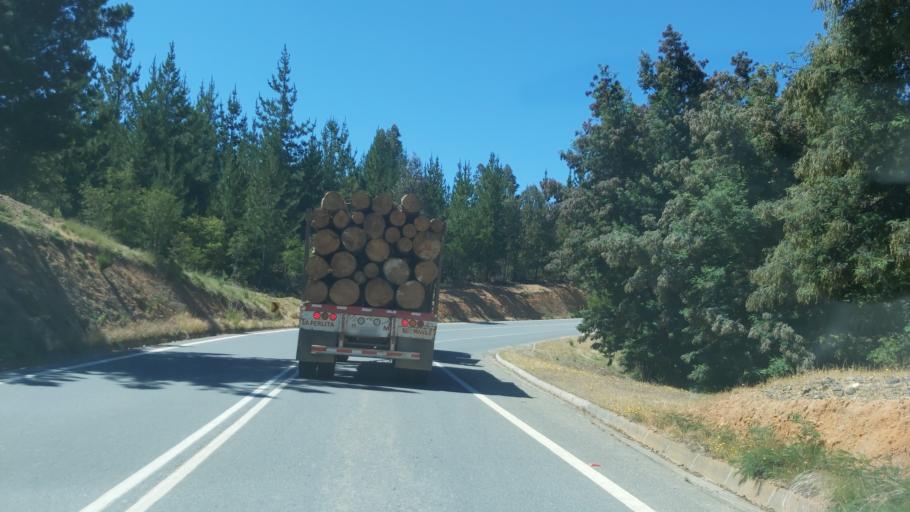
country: CL
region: Maule
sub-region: Provincia de Talca
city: Constitucion
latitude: -34.9261
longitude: -71.9873
